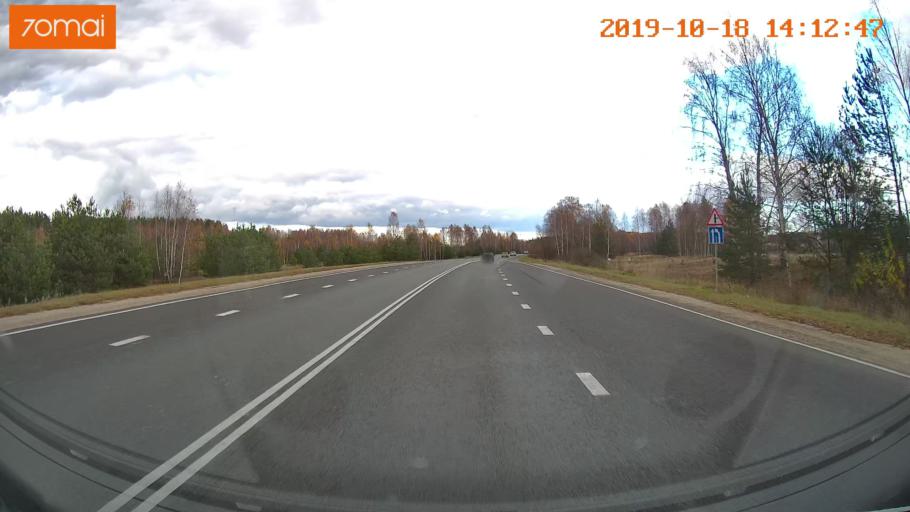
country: RU
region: Rjazan
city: Spas-Klepiki
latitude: 55.1485
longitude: 40.2572
